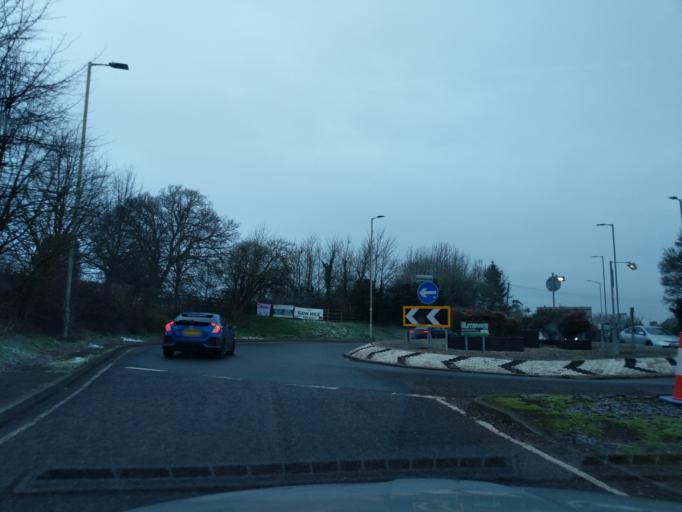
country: GB
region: England
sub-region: Hertfordshire
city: Kings Langley
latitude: 51.7059
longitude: -0.4456
